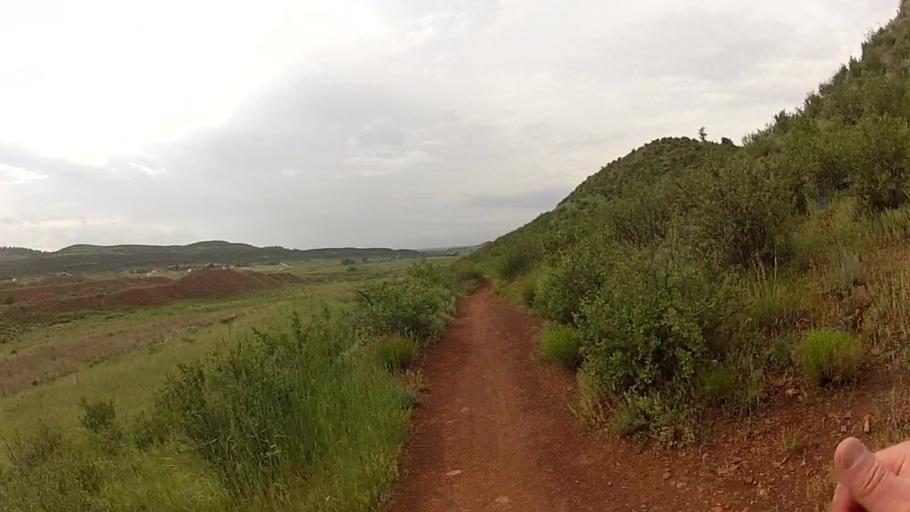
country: US
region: Colorado
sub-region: Larimer County
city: Loveland
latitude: 40.4204
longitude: -105.1575
